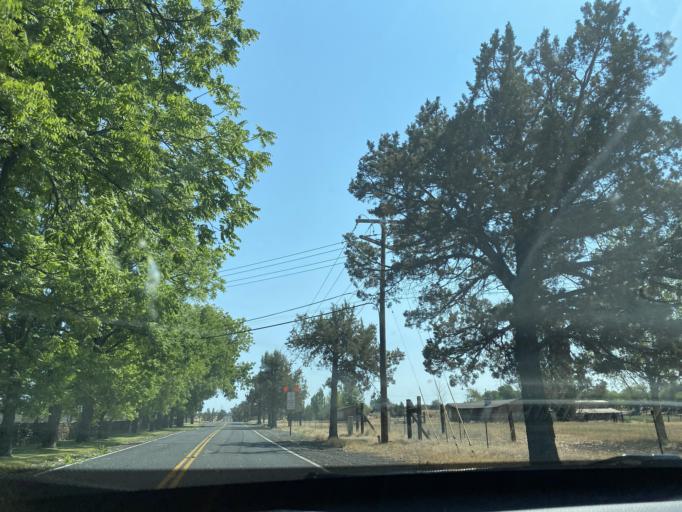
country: US
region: Oregon
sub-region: Deschutes County
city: Terrebonne
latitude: 44.3666
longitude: -121.1585
